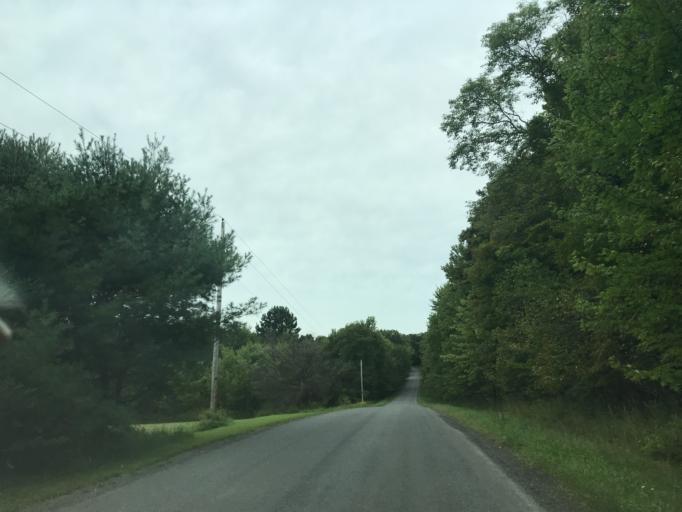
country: US
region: New York
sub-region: Otsego County
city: Worcester
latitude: 42.5237
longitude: -74.6631
